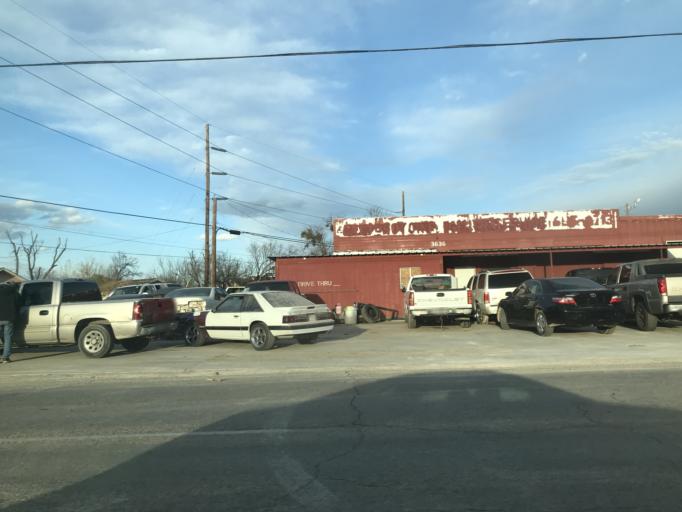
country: US
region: Texas
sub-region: Tom Green County
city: San Angelo
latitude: 31.4972
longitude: -100.4593
